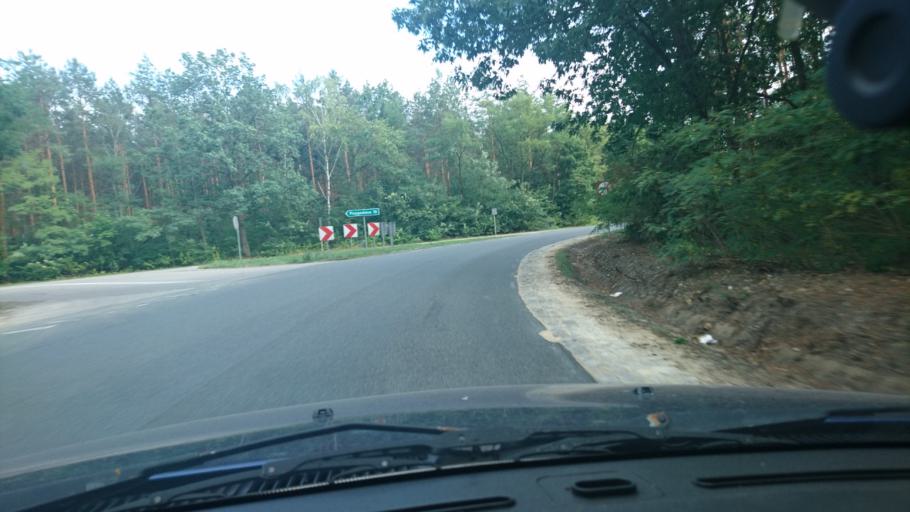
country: PL
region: Greater Poland Voivodeship
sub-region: Powiat ostrowski
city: Jankow Przygodzki
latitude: 51.5205
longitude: 17.7660
